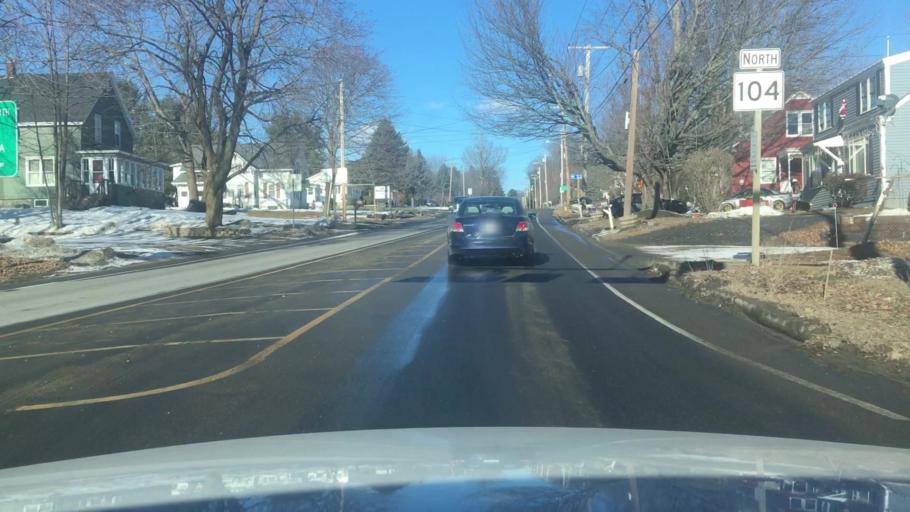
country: US
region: Maine
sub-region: Kennebec County
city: Waterville
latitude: 44.5725
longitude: -69.6413
